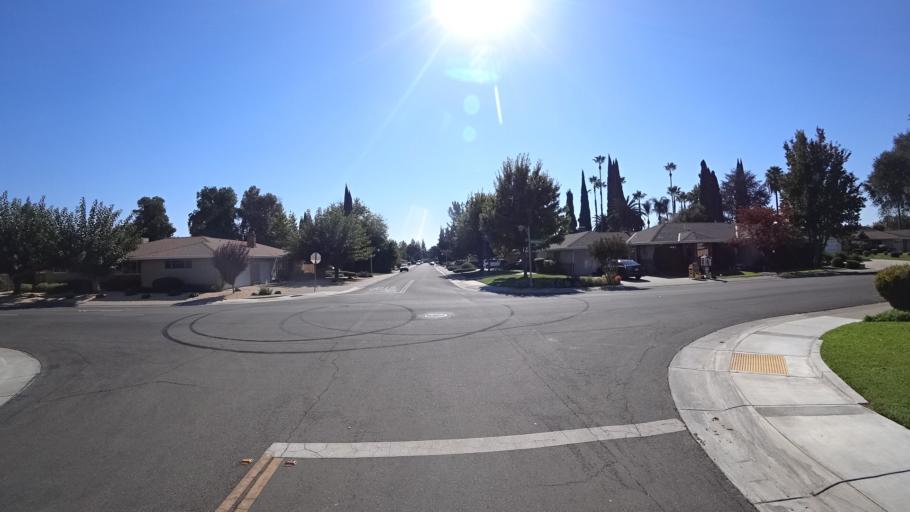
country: US
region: California
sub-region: Sacramento County
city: Parkway
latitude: 38.4993
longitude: -121.5217
